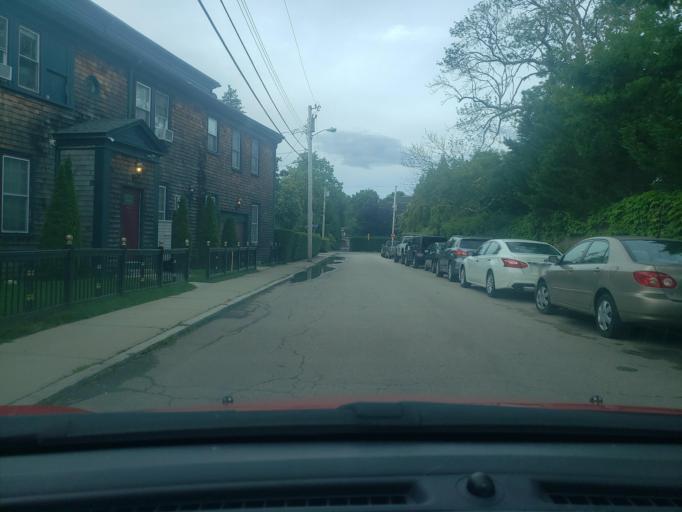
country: US
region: Rhode Island
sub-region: Newport County
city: Newport
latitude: 41.4806
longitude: -71.3064
